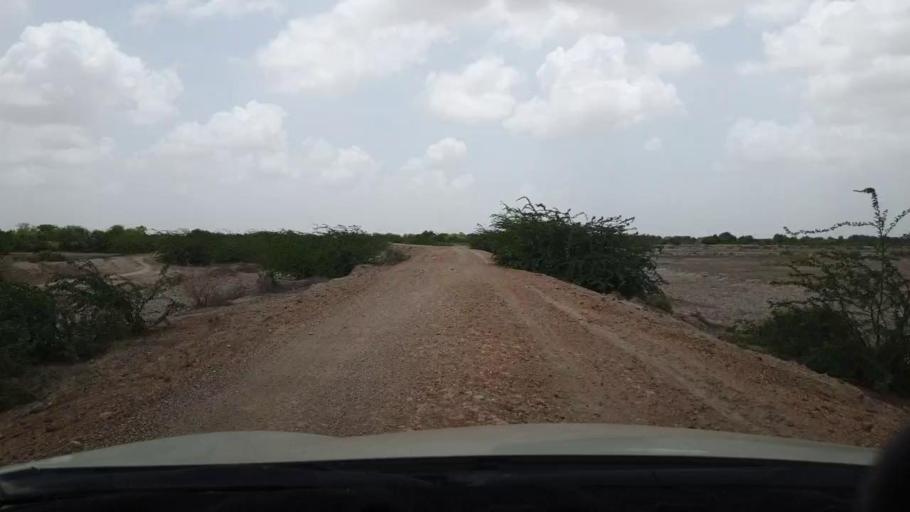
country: PK
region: Sindh
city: Kadhan
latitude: 24.3734
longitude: 68.9280
